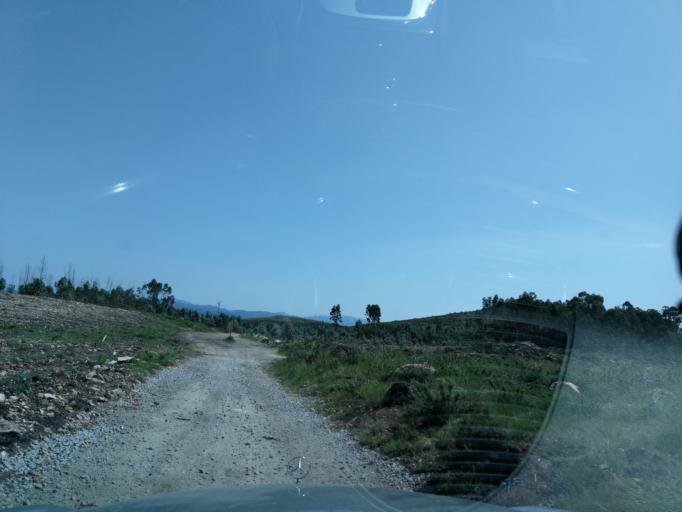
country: PT
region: Braga
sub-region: Povoa de Lanhoso
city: Povoa de Lanhoso
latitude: 41.5675
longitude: -8.3372
